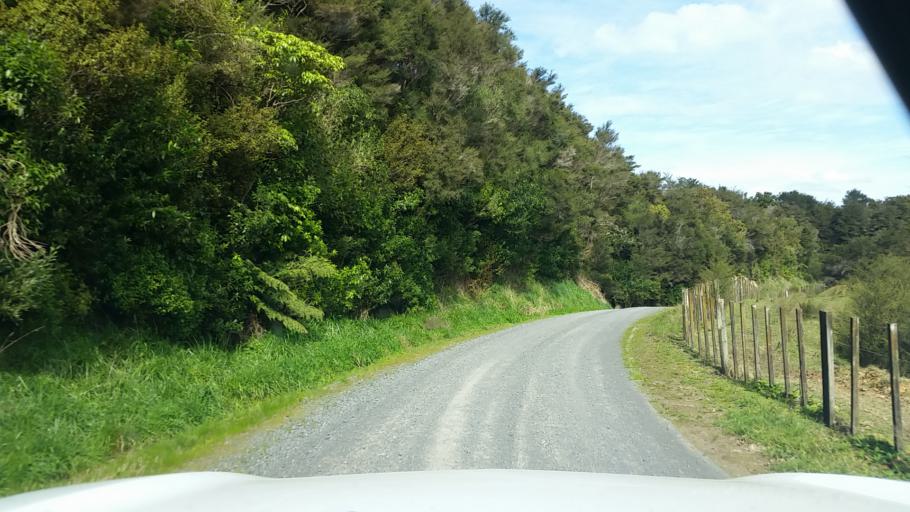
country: NZ
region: Waikato
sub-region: Hauraki District
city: Ngatea
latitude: -37.4765
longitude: 175.4558
